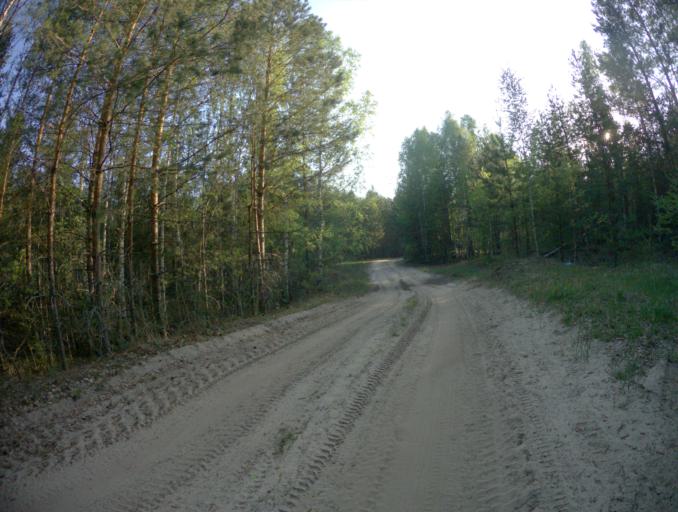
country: RU
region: Vladimir
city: Vyazniki
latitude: 56.3649
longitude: 42.1502
